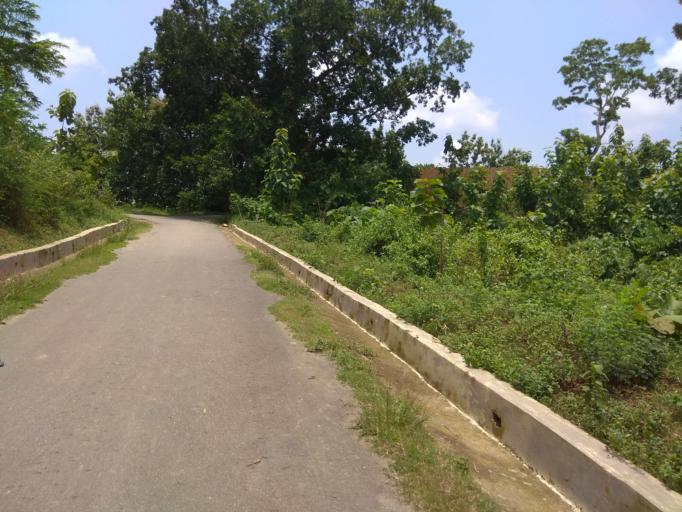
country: BD
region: Chittagong
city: Manikchari
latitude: 22.8857
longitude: 91.9218
